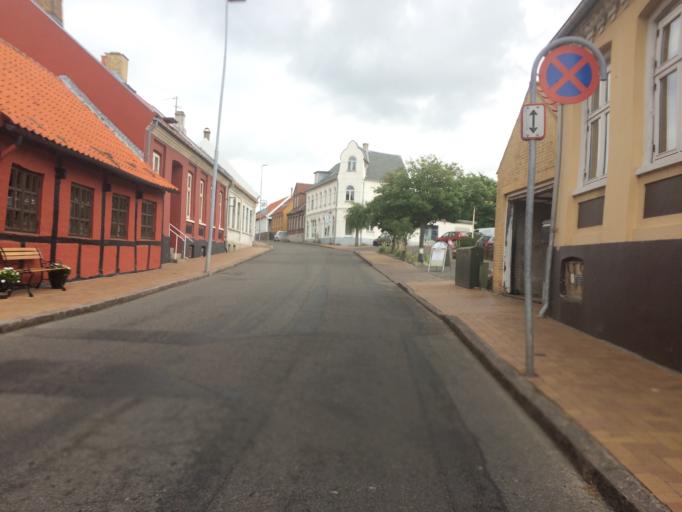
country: DK
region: Capital Region
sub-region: Bornholm Kommune
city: Ronne
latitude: 55.1854
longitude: 14.7061
